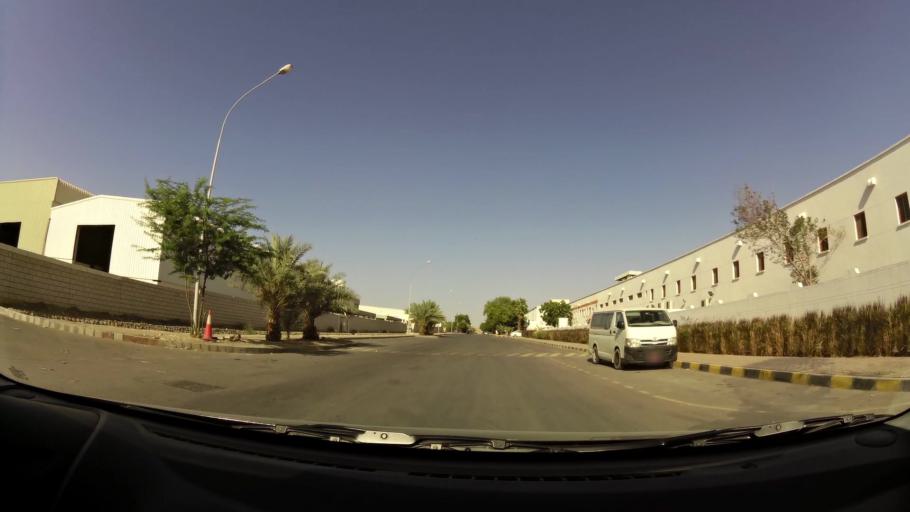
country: OM
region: Muhafazat Masqat
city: As Sib al Jadidah
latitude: 23.5520
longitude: 58.2202
